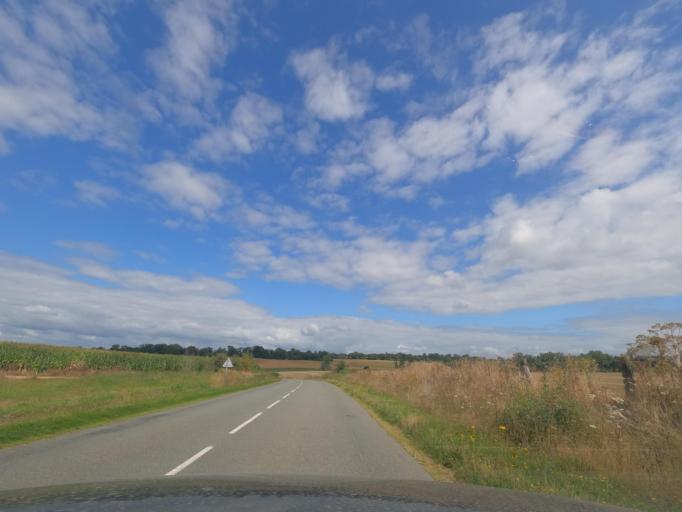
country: FR
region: Pays de la Loire
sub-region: Departement de la Mayenne
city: Landivy
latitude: 48.4637
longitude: -1.0494
